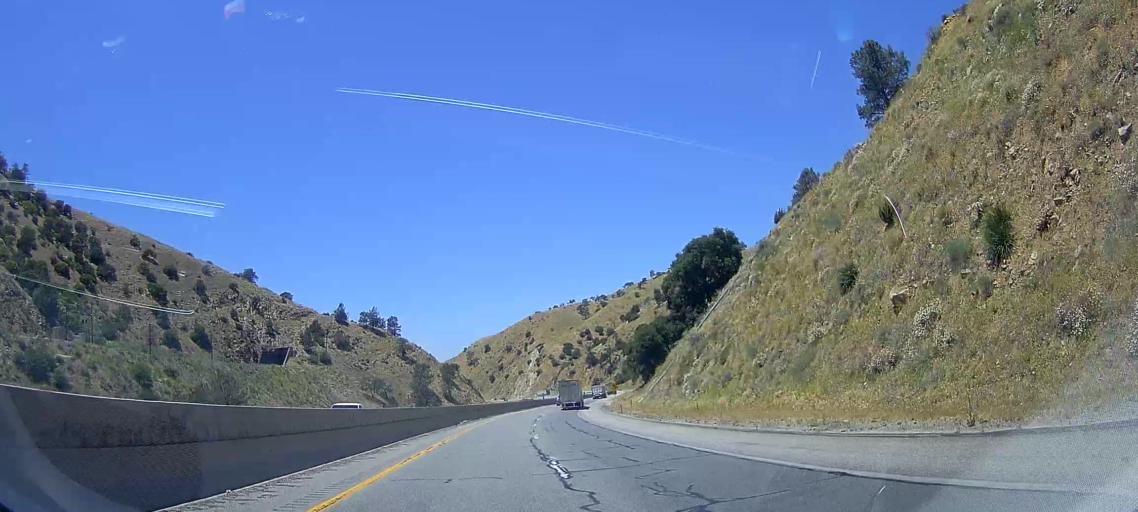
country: US
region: California
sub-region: Kern County
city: Golden Hills
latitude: 35.1794
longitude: -118.4861
